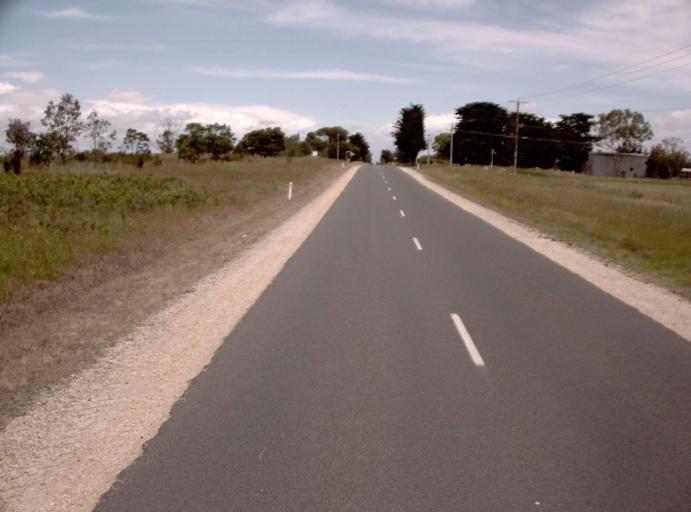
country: AU
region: Victoria
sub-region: Wellington
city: Sale
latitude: -37.9779
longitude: 147.0373
